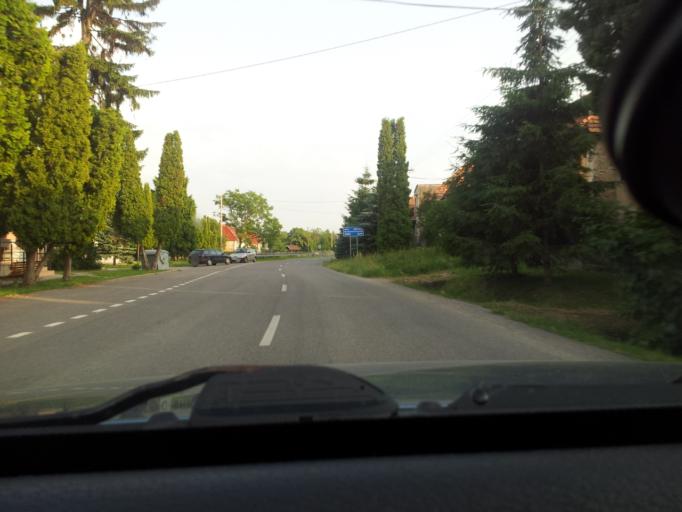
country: SK
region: Banskobystricky
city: Nova Bana
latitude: 48.3218
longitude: 18.7046
